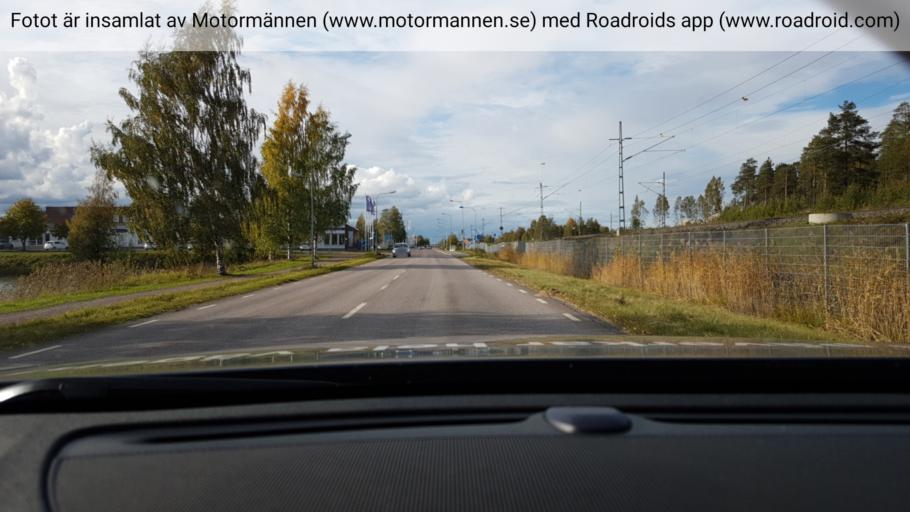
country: SE
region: Norrbotten
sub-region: Lulea Kommun
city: Bergnaset
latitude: 65.6076
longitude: 22.1277
